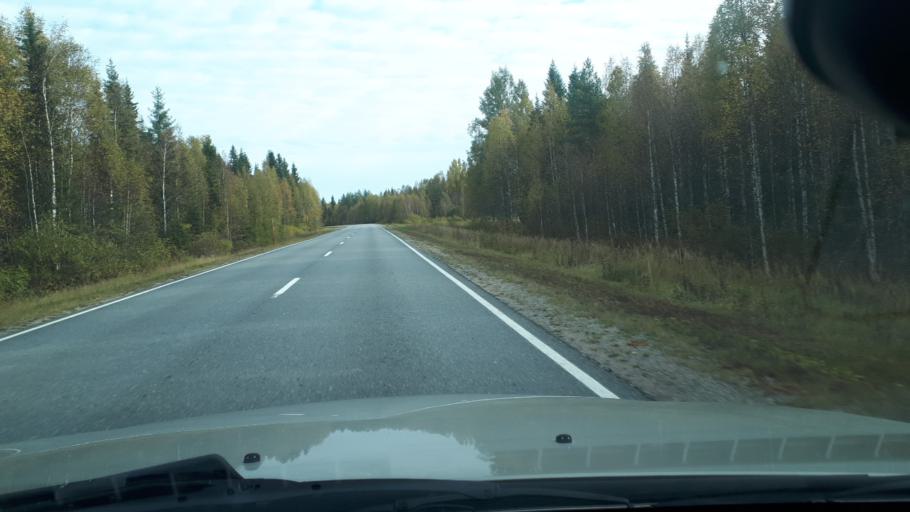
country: FI
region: Lapland
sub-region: Rovaniemi
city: Rovaniemi
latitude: 65.9579
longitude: 25.9394
